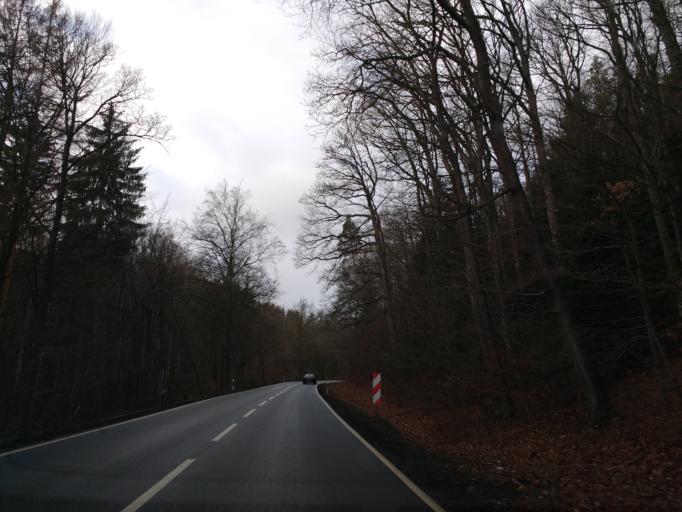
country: DE
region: Saxony-Anhalt
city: Bad Suderode
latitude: 51.7129
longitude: 11.0984
